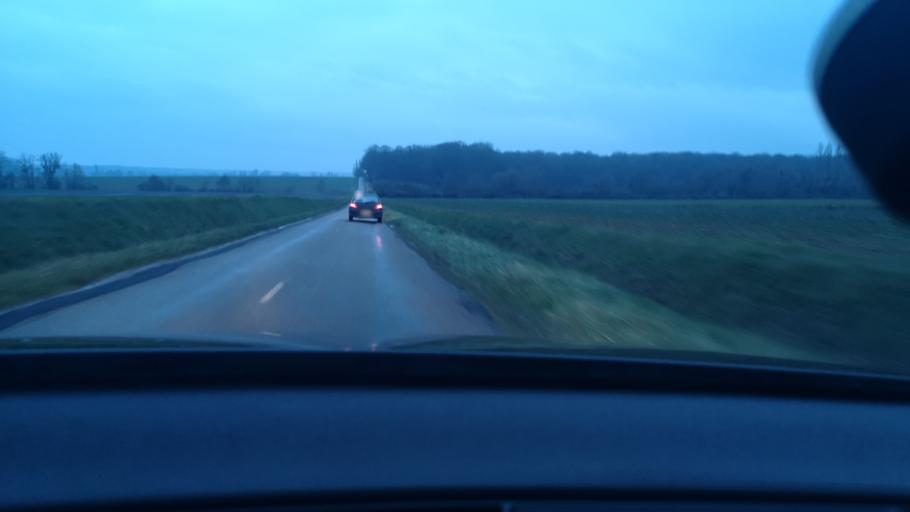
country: FR
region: Bourgogne
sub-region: Departement de Saone-et-Loire
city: Gergy
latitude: 46.9706
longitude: 4.9306
